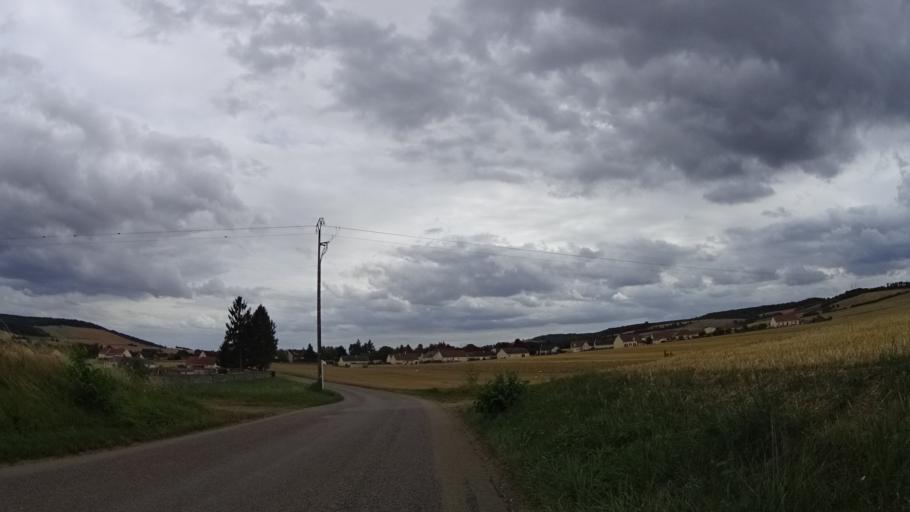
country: FR
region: Bourgogne
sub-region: Departement de l'Yonne
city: Cezy
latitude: 47.9622
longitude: 3.3577
